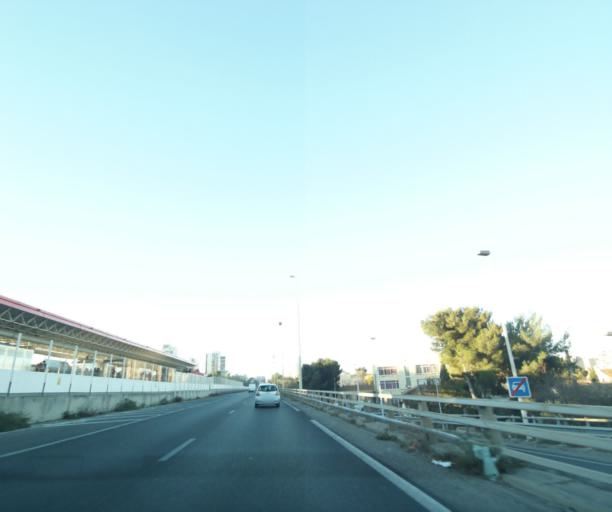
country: FR
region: Provence-Alpes-Cote d'Azur
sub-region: Departement des Bouches-du-Rhone
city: Marseille 13
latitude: 43.3214
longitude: 5.4166
